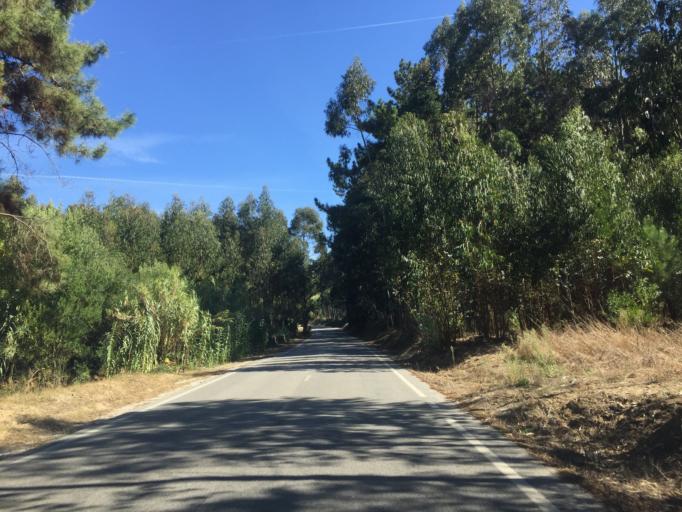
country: PT
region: Coimbra
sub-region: Figueira da Foz
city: Buarcos
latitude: 40.2159
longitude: -8.8760
